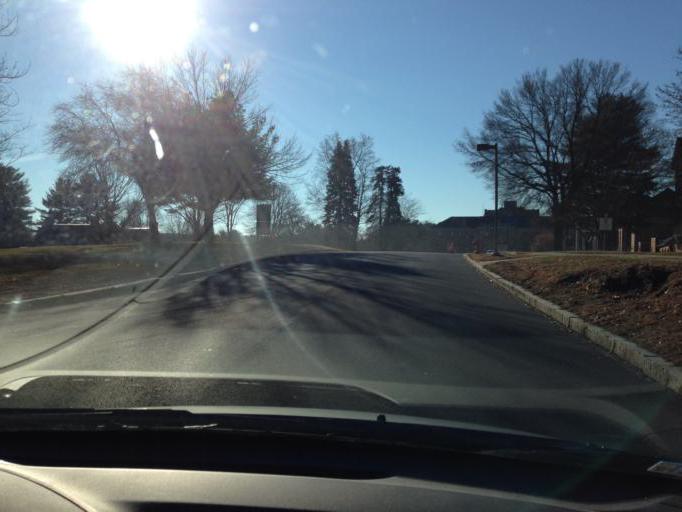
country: US
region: Massachusetts
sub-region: Middlesex County
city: Bedford
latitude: 42.5068
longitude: -71.2733
